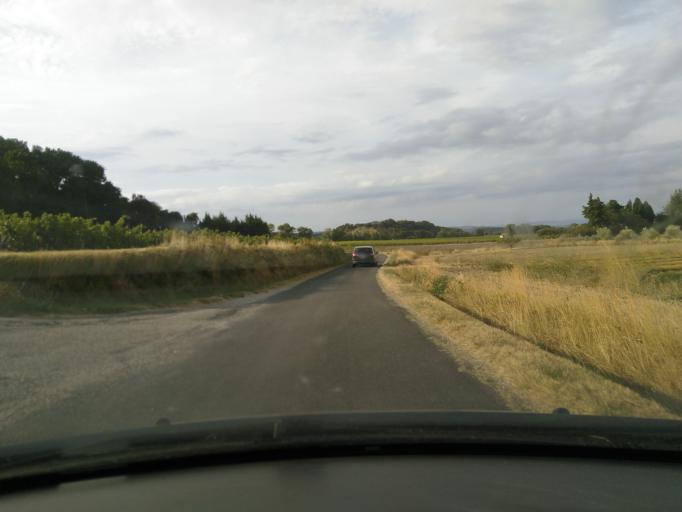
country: FR
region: Rhone-Alpes
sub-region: Departement de la Drome
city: Taulignan
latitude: 44.4259
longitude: 5.0492
